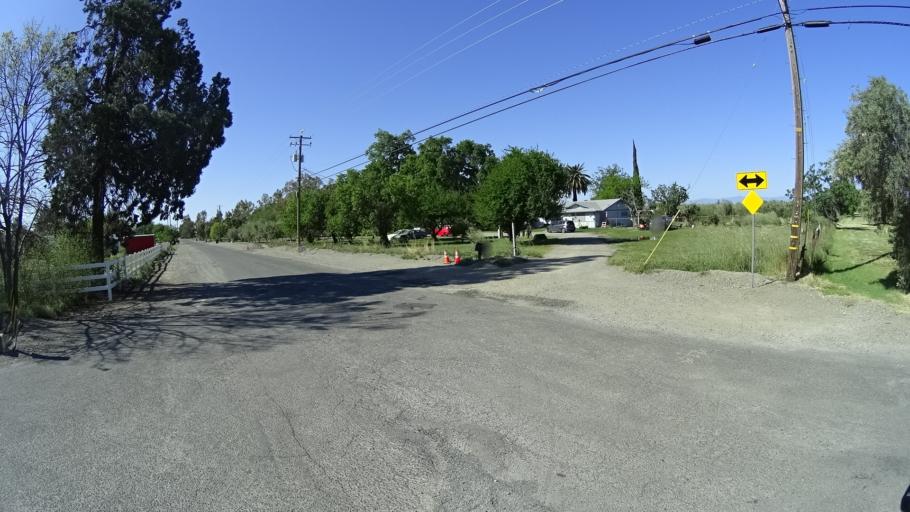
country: US
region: California
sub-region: Glenn County
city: Orland
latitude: 39.7290
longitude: -122.1689
